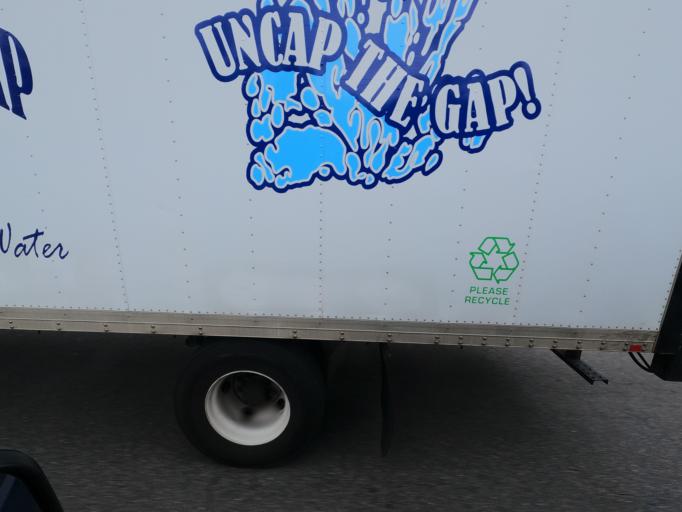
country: US
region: Tennessee
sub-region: Sullivan County
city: Kingsport
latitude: 36.5554
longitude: -82.5968
